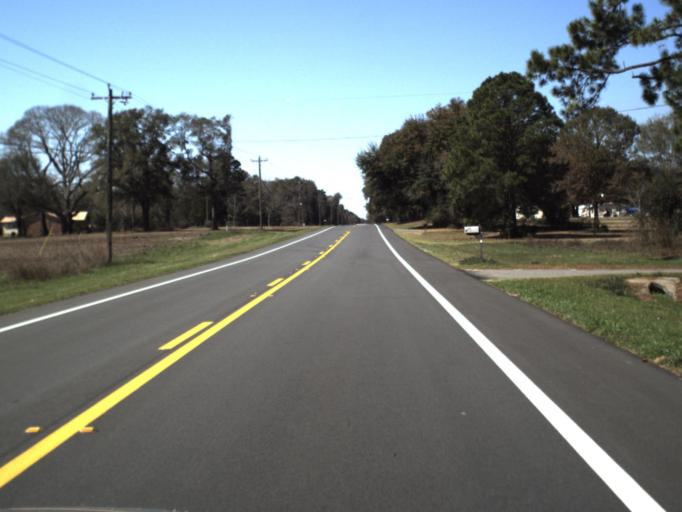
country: US
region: Florida
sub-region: Jackson County
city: Malone
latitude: 30.8649
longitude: -85.1172
